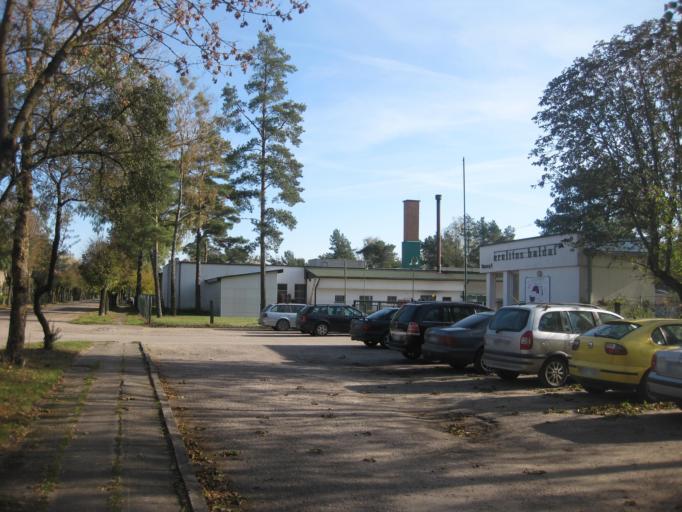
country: LT
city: Ezerelis
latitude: 54.8834
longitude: 23.5931
